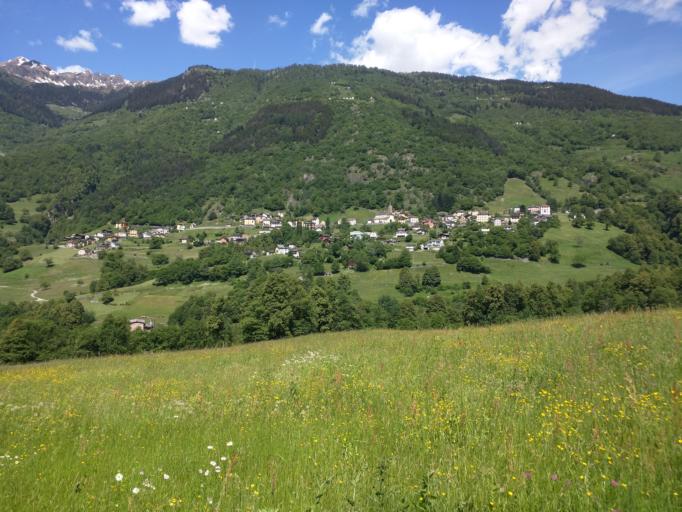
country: CH
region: Ticino
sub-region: Blenio District
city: Acquarossa
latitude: 46.4775
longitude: 8.9431
